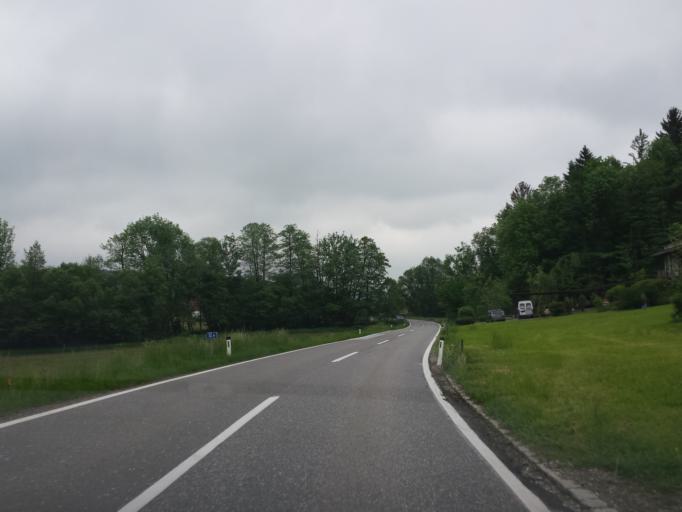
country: AT
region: Styria
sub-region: Politischer Bezirk Graz-Umgebung
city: Kumberg
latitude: 47.1434
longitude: 15.5439
